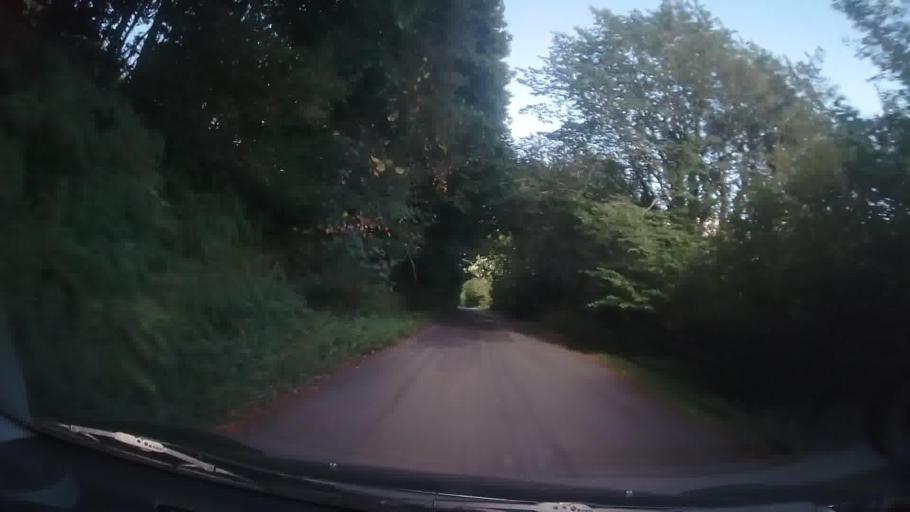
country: GB
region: Wales
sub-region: Caerphilly County Borough
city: Rhymney
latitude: 51.8543
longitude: -3.3195
